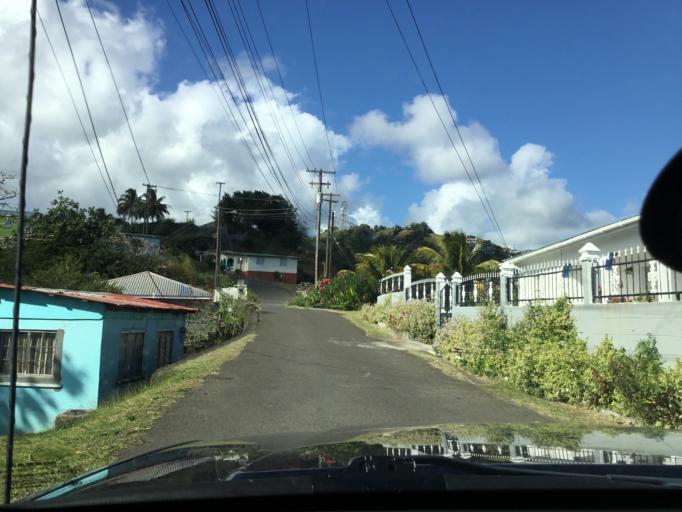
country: VC
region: Saint George
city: Kingstown
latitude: 13.1554
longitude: -61.1775
